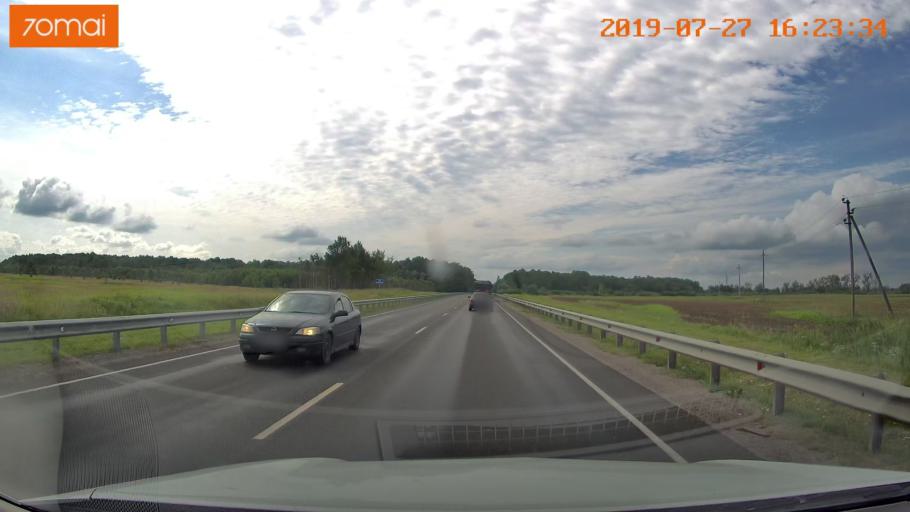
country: RU
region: Kaliningrad
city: Zheleznodorozhnyy
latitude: 54.6312
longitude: 21.4710
